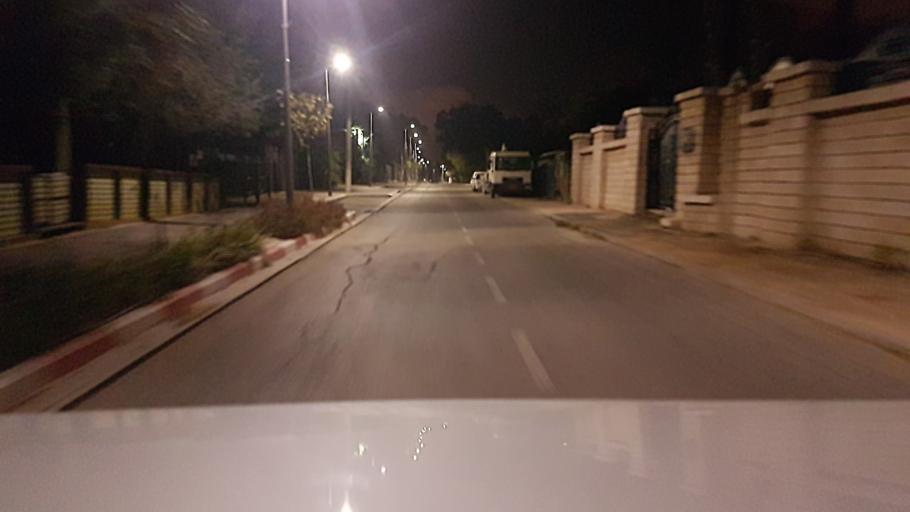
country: IL
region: Central District
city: Nehalim
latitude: 32.0775
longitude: 34.9280
